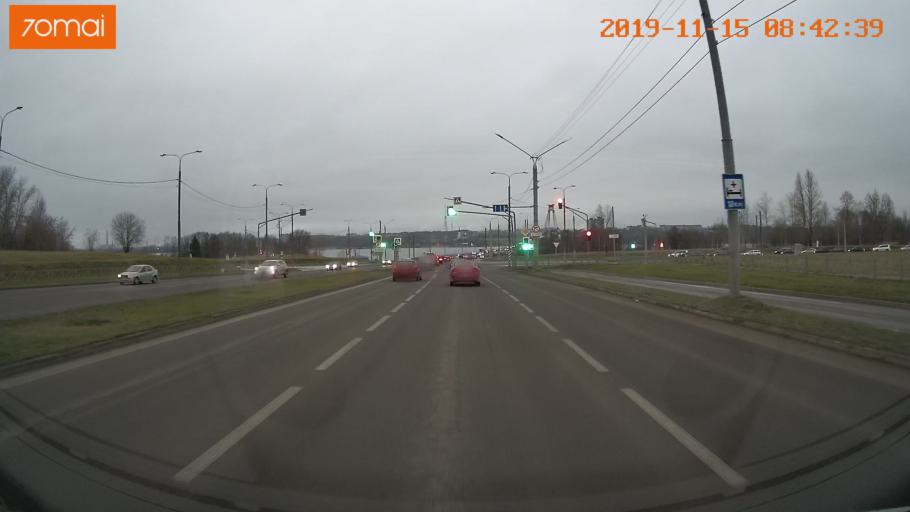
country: RU
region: Vologda
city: Cherepovets
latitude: 59.1043
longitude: 37.9070
